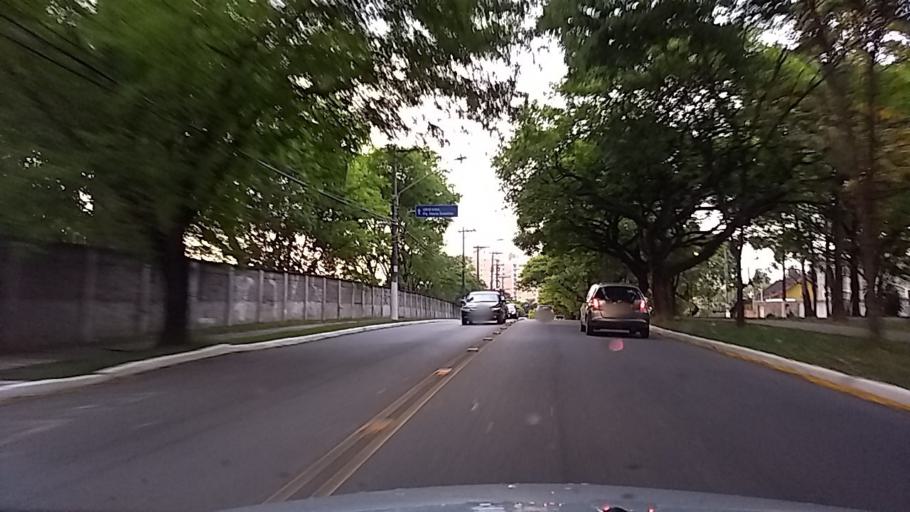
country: BR
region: Sao Paulo
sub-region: Osasco
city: Osasco
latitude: -23.4915
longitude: -46.7372
